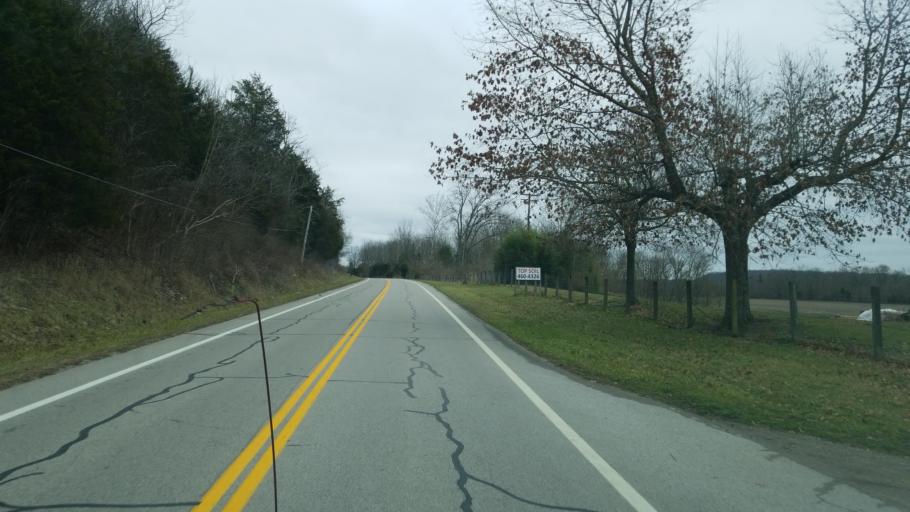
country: US
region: Kentucky
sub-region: Bracken County
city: Brooksville
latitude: 38.8004
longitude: -84.1586
